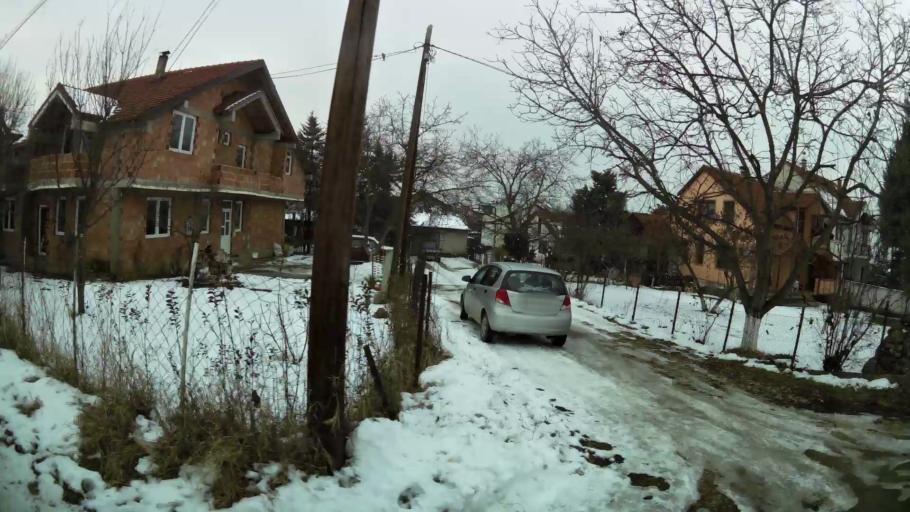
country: MK
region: Butel
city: Butel
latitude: 42.0377
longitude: 21.4542
